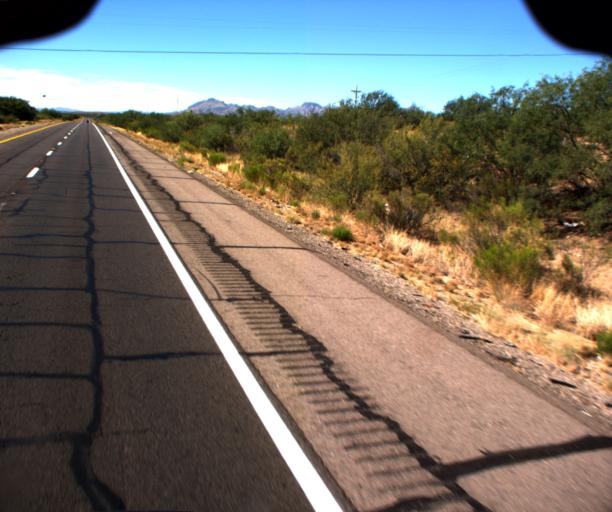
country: US
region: Arizona
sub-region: Pima County
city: Arivaca Junction
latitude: 31.6900
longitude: -111.0650
